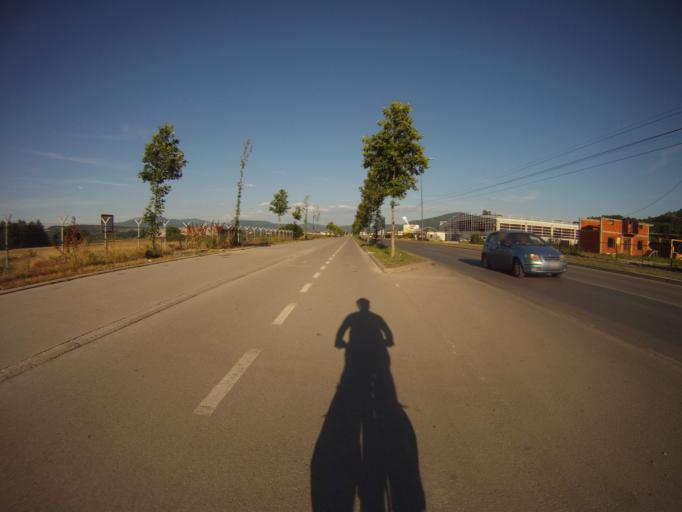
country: RS
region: Central Serbia
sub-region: Nisavski Okrug
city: Nis
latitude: 43.3090
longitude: 21.9439
